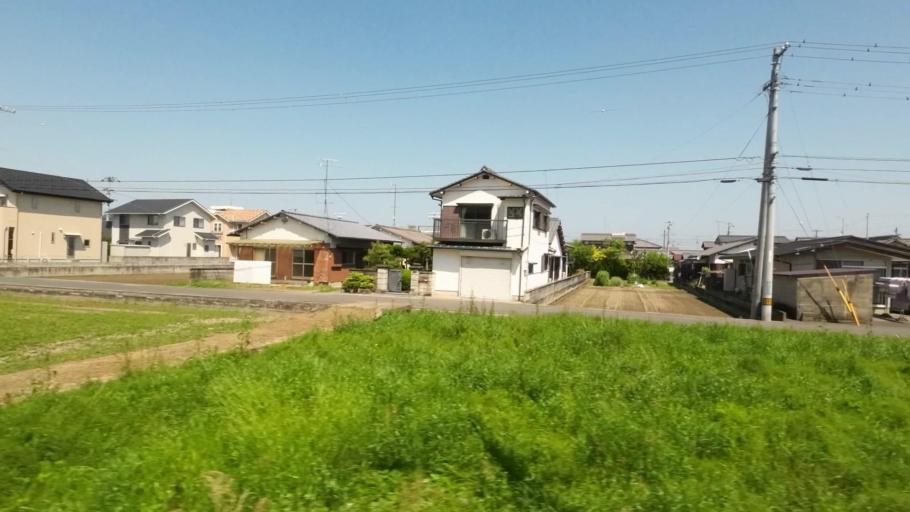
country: JP
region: Ehime
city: Niihama
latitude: 33.9663
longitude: 133.3175
